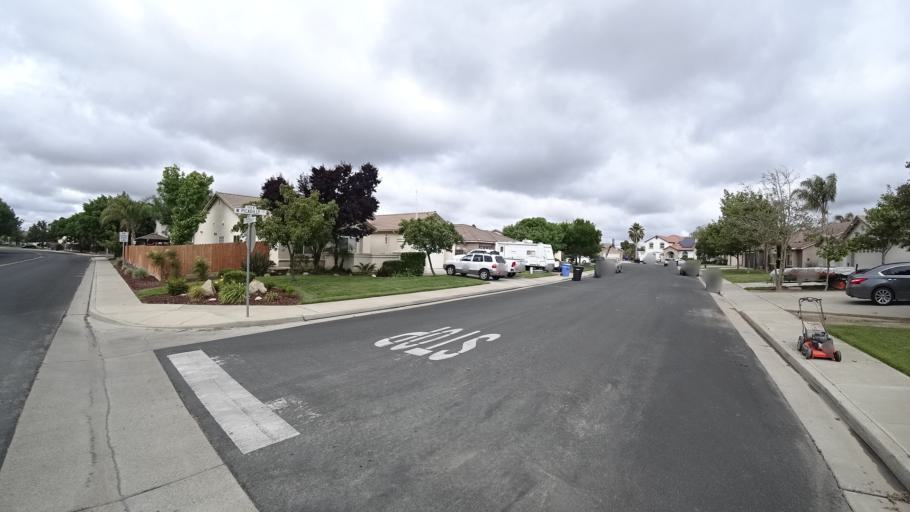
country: US
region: California
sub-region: Kings County
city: Hanford
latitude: 36.3445
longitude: -119.6692
